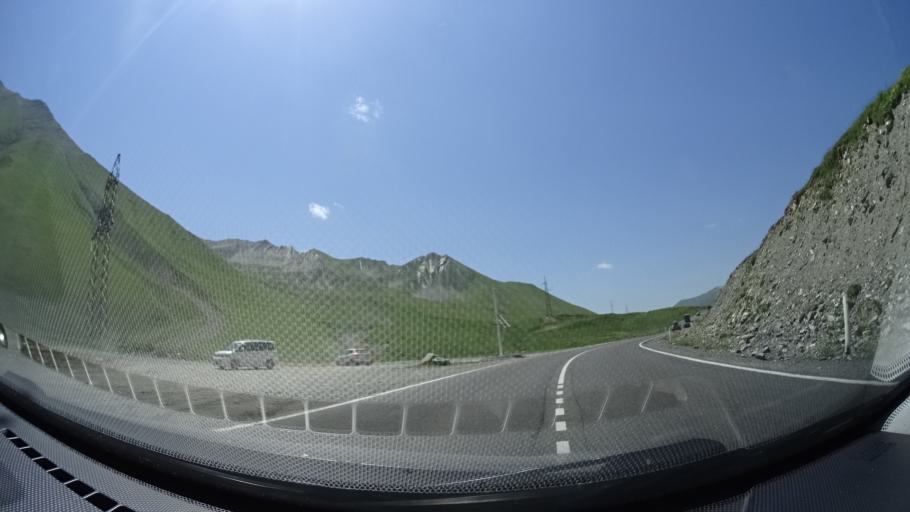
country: GE
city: Gudauri
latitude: 42.5198
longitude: 44.4677
